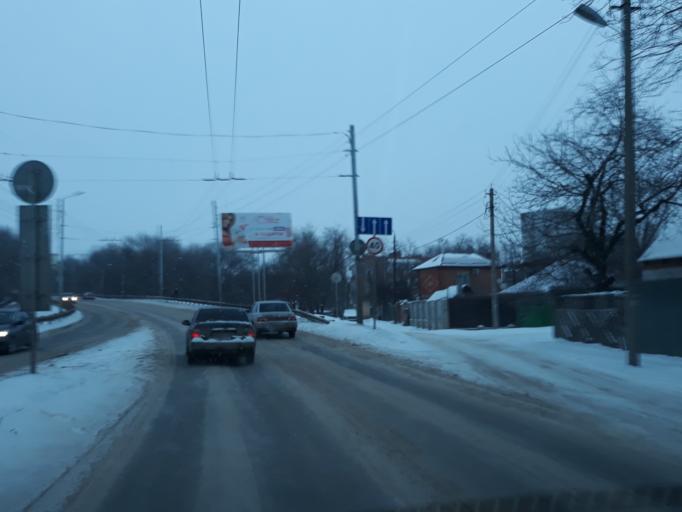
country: RU
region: Rostov
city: Taganrog
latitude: 47.2628
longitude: 38.9262
